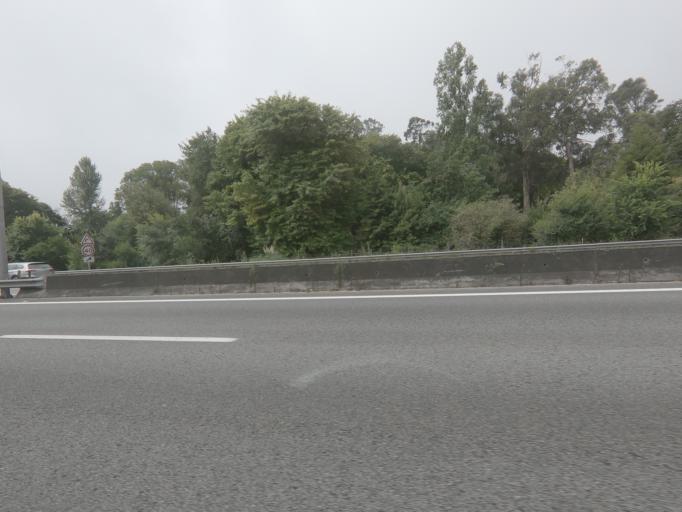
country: PT
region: Porto
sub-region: Matosinhos
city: Leca da Palmeira
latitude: 41.1982
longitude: -8.6857
